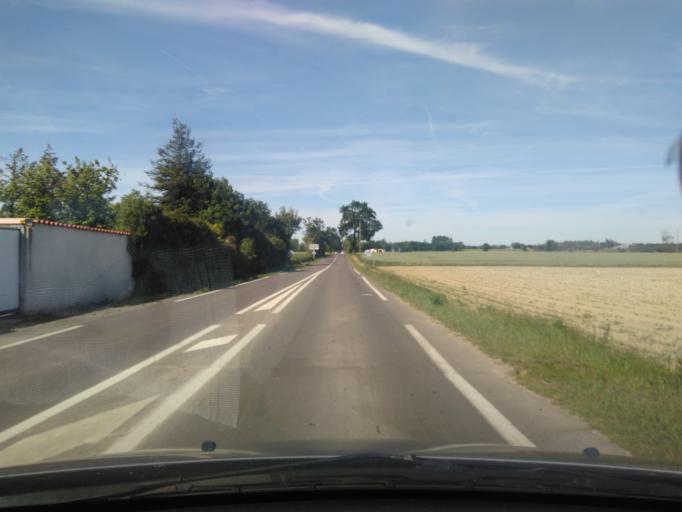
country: FR
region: Pays de la Loire
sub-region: Departement de la Vendee
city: Nieul-le-Dolent
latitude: 46.5254
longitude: -1.5515
